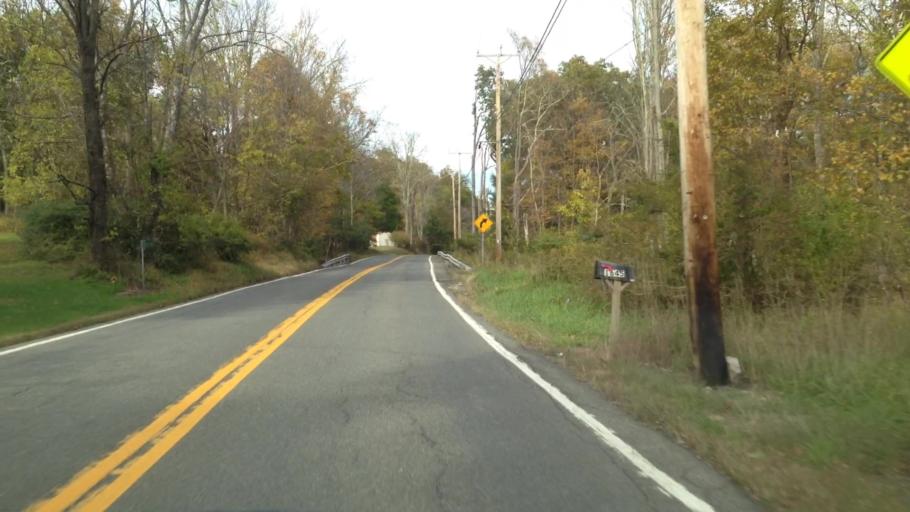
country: US
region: New York
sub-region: Ulster County
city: Rosendale Village
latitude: 41.8562
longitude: -74.0335
